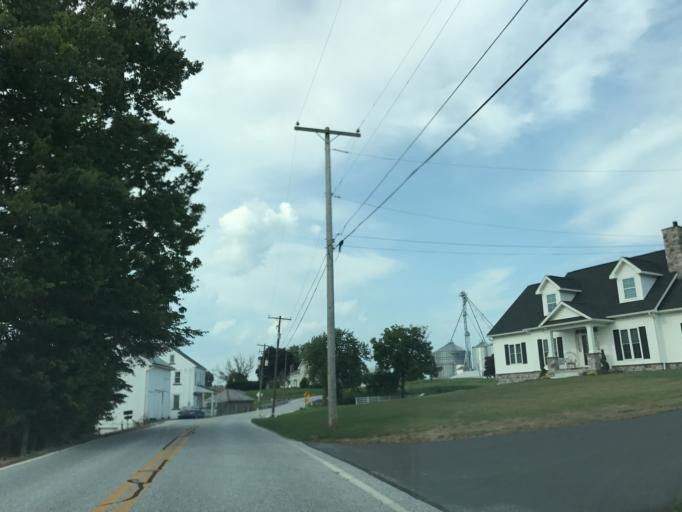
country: US
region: Pennsylvania
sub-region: Lancaster County
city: Mount Joy
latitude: 40.1016
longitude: -76.5349
